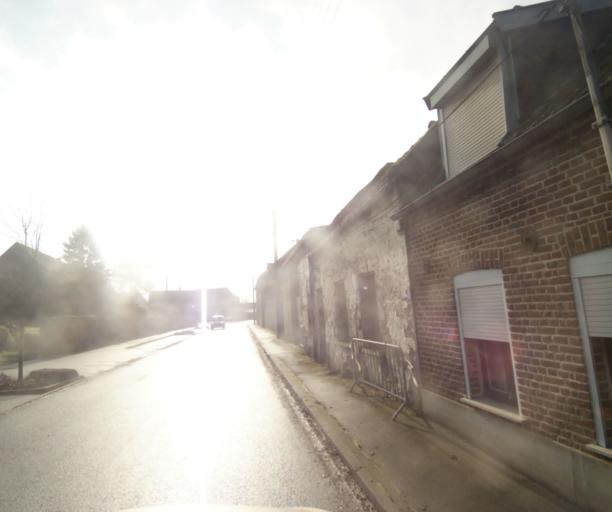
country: FR
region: Nord-Pas-de-Calais
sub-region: Departement du Nord
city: Thiant
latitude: 50.2878
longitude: 3.4554
